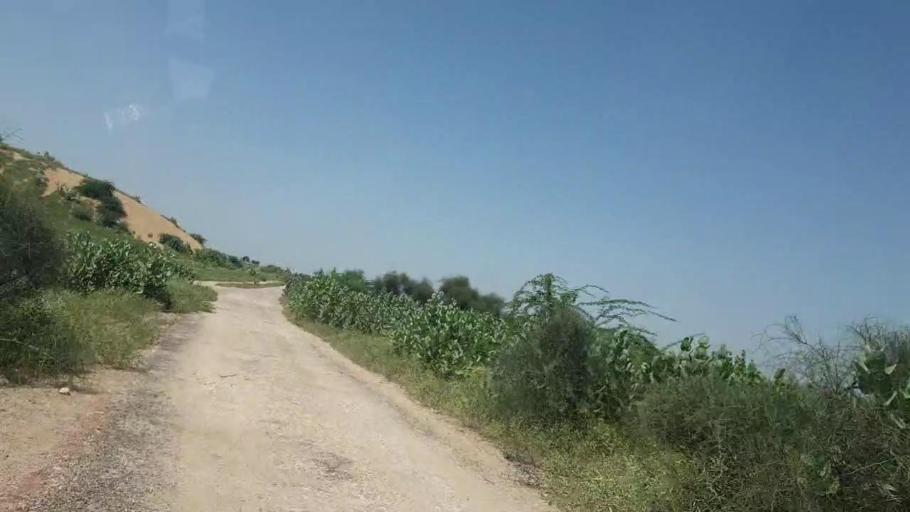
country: PK
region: Sindh
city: Chor
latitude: 25.3553
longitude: 70.3350
